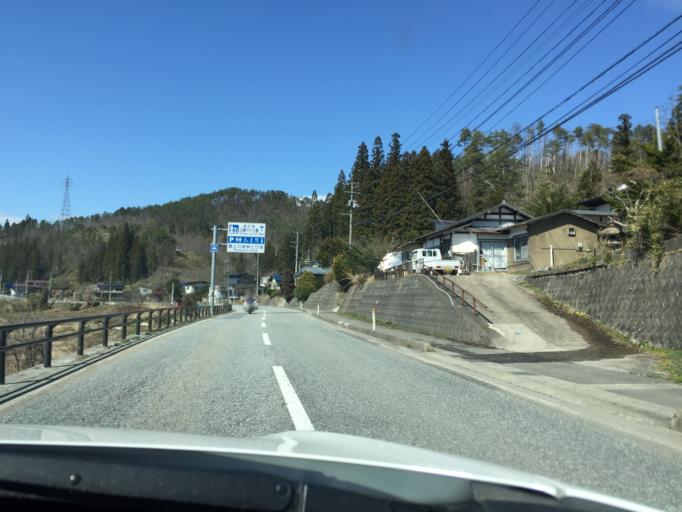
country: JP
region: Yamagata
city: Nagai
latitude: 38.2009
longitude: 140.1039
